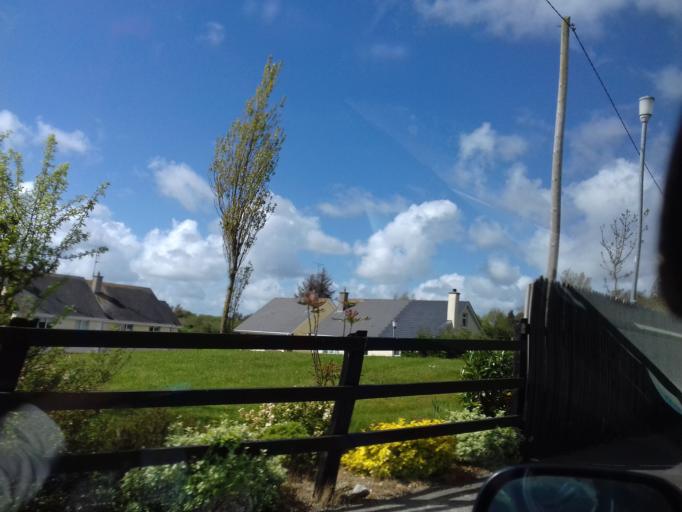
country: IE
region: Leinster
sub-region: Loch Garman
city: Castlebridge
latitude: 52.3932
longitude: -6.3927
